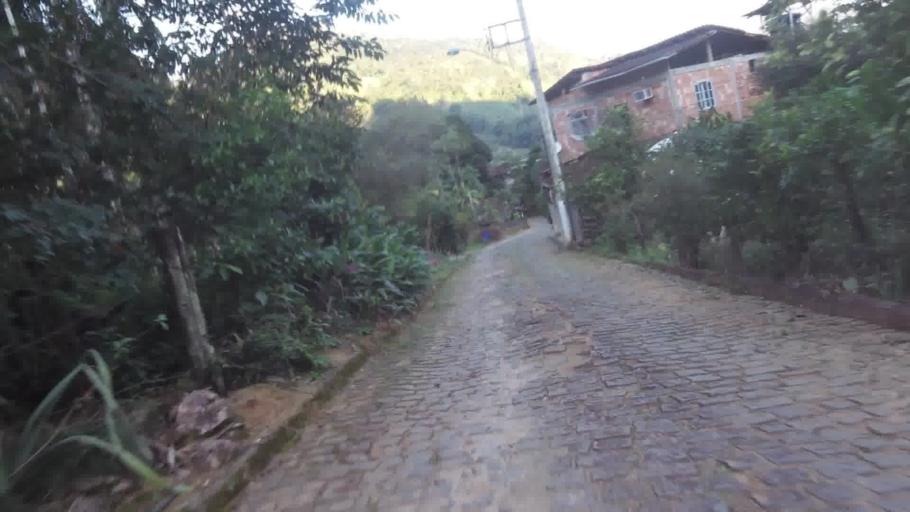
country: BR
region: Espirito Santo
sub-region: Alfredo Chaves
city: Alfredo Chaves
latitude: -20.5775
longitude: -40.7004
